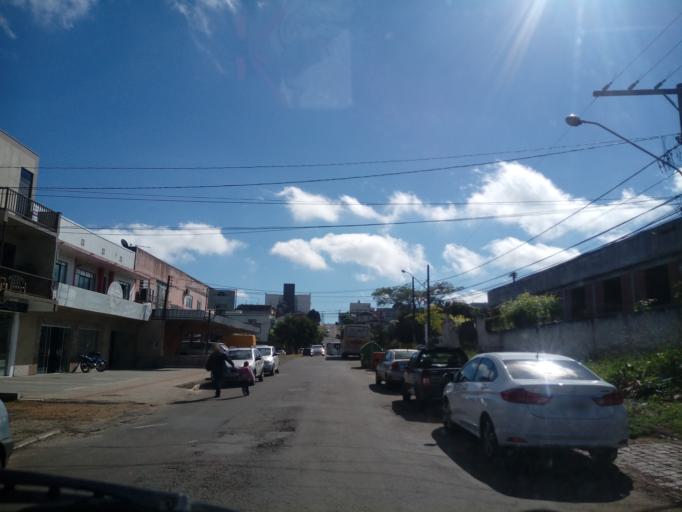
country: BR
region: Santa Catarina
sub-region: Chapeco
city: Chapeco
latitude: -27.1089
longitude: -52.6035
